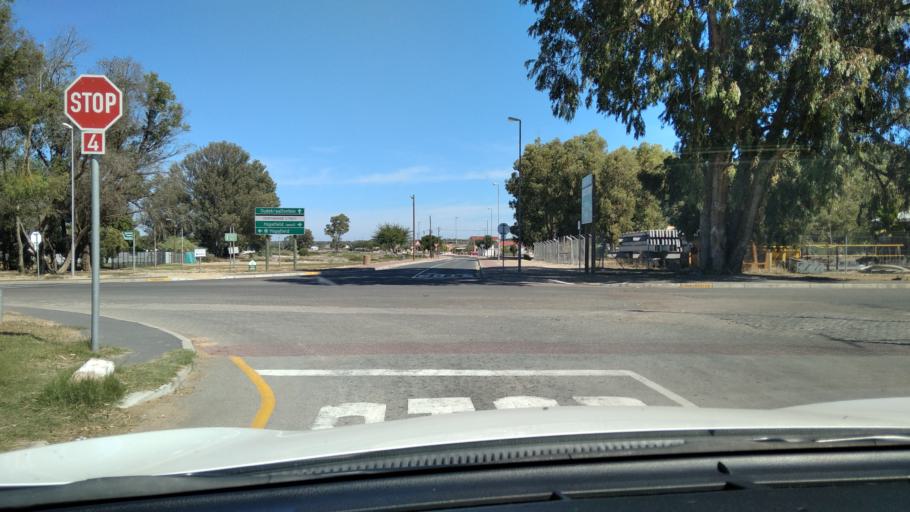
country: ZA
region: Western Cape
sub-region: West Coast District Municipality
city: Moorreesburg
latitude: -33.0597
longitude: 18.3418
